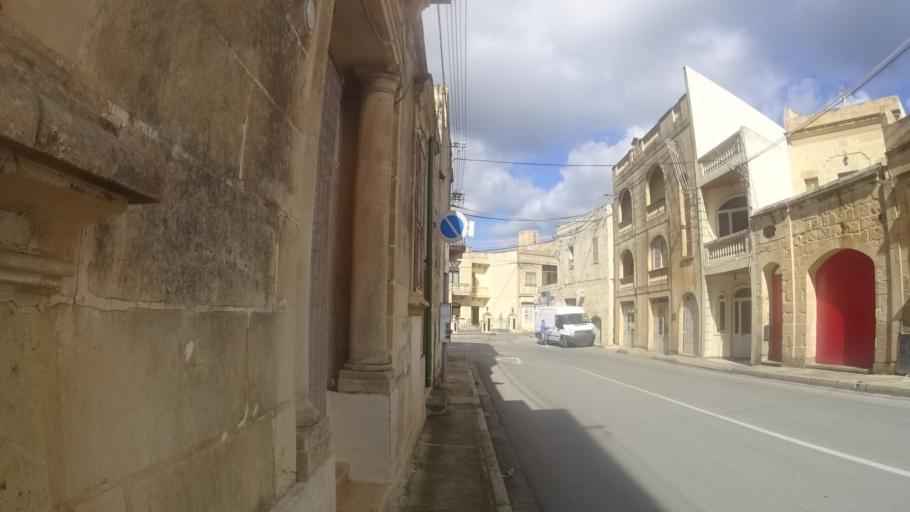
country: MT
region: In-Nadur
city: Nadur
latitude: 36.0395
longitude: 14.2885
